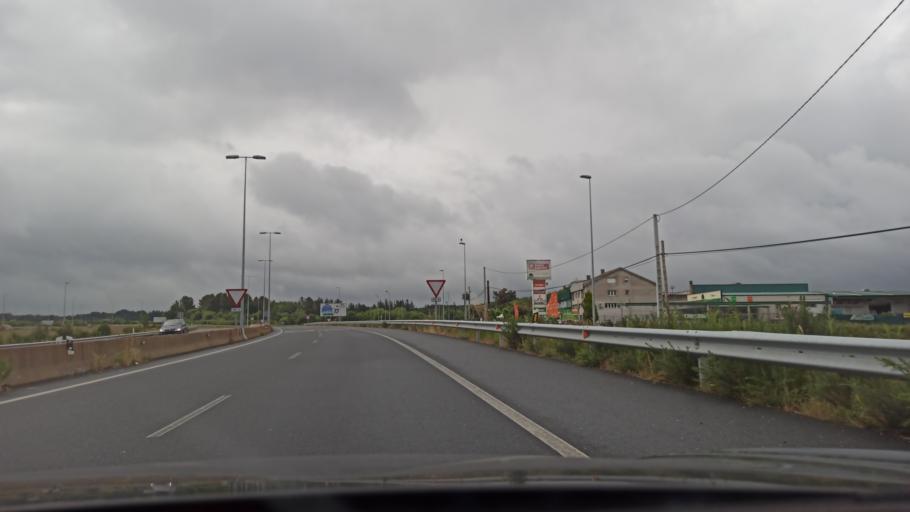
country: ES
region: Galicia
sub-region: Provincia de Lugo
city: Lugo
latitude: 42.9829
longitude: -7.5875
